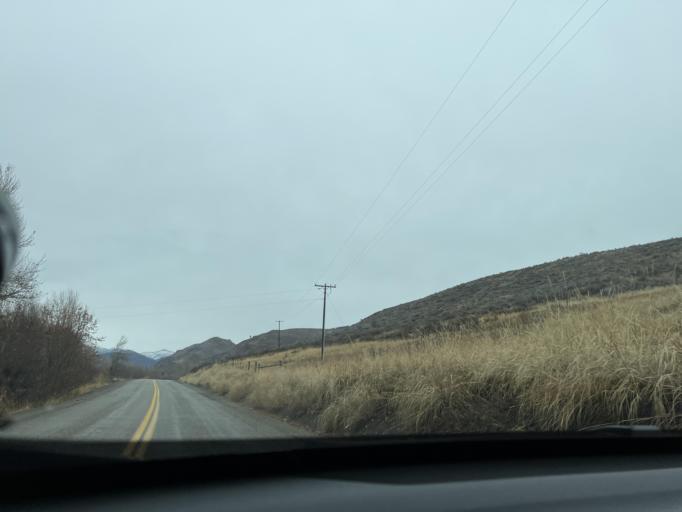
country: US
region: Washington
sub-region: Okanogan County
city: Brewster
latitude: 48.5043
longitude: -120.1738
